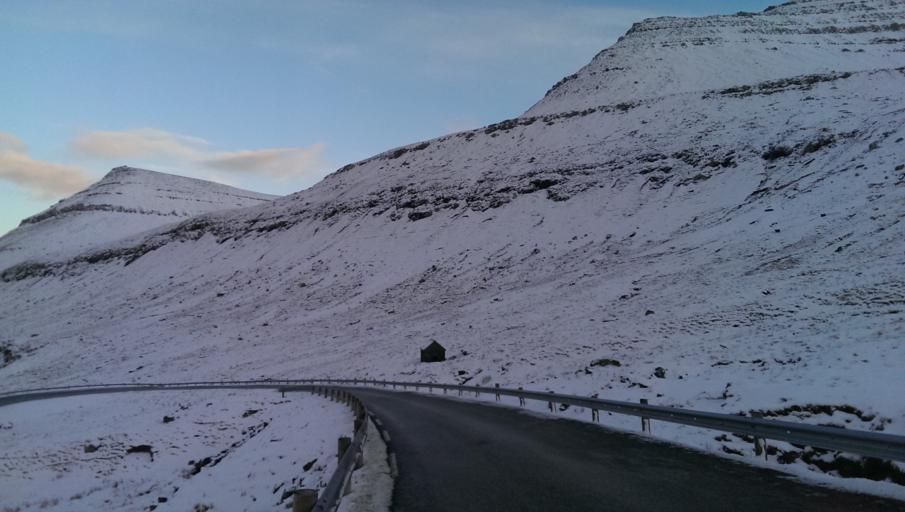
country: FO
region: Eysturoy
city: Fuglafjordur
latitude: 62.2542
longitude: -6.8608
